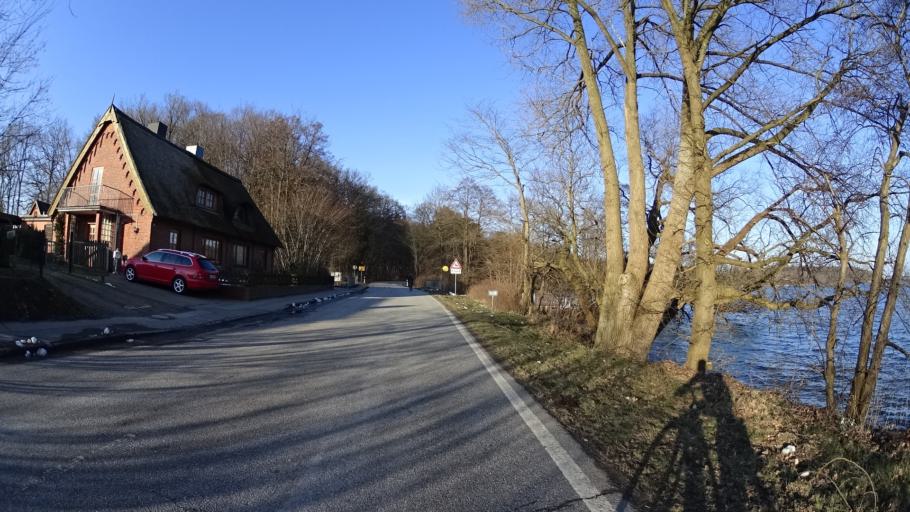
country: DE
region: Schleswig-Holstein
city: Fargau-Pratjau
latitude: 54.3215
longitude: 10.3881
